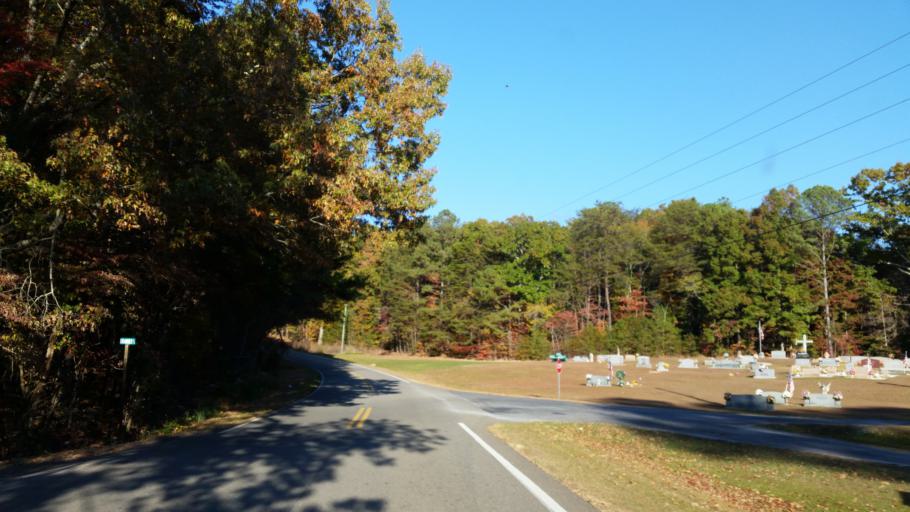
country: US
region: Georgia
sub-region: Pickens County
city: Jasper
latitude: 34.5744
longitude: -84.4595
